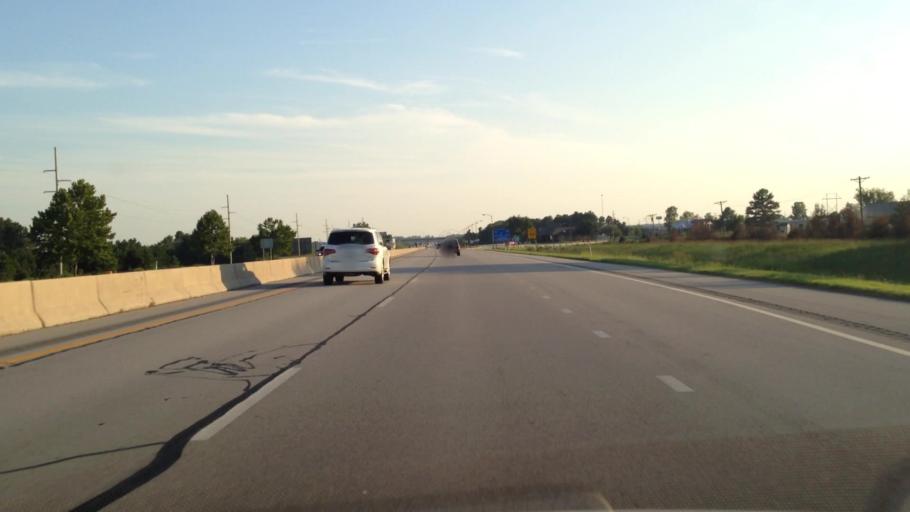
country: US
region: Oklahoma
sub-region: Ottawa County
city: Miami
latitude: 36.8788
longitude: -94.8439
